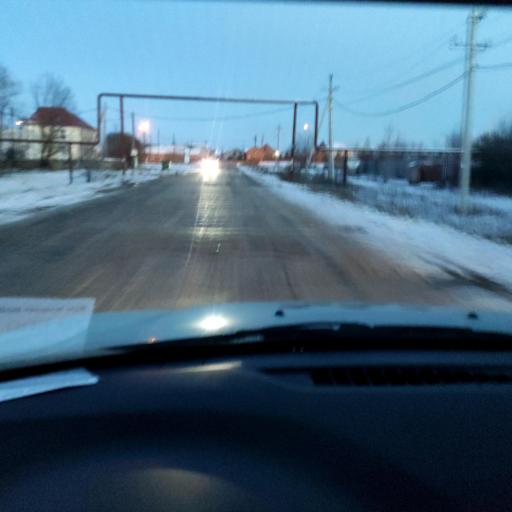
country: RU
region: Samara
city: Tol'yatti
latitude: 53.5689
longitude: 49.3951
